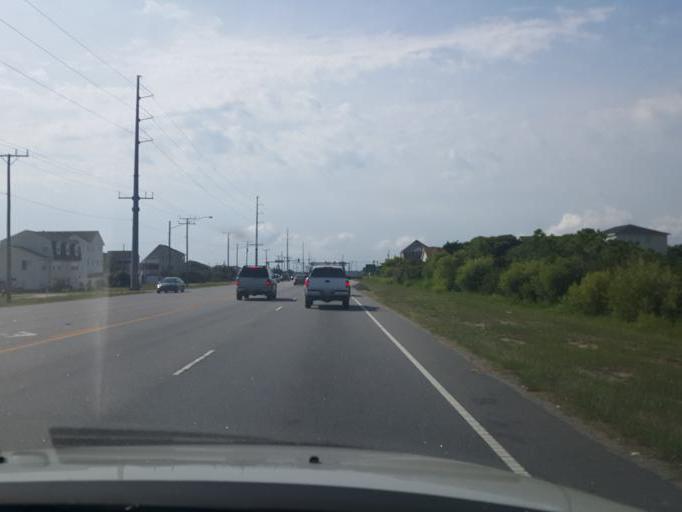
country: US
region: North Carolina
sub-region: Dare County
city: Kill Devil Hills
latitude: 36.0155
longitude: -75.6621
